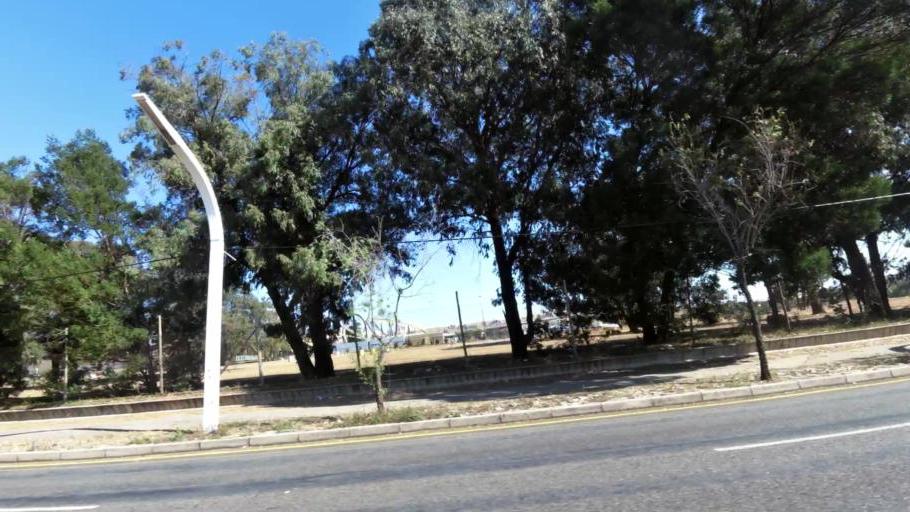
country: ZA
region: Gauteng
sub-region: City of Johannesburg Metropolitan Municipality
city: Johannesburg
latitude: -26.2406
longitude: 27.9855
